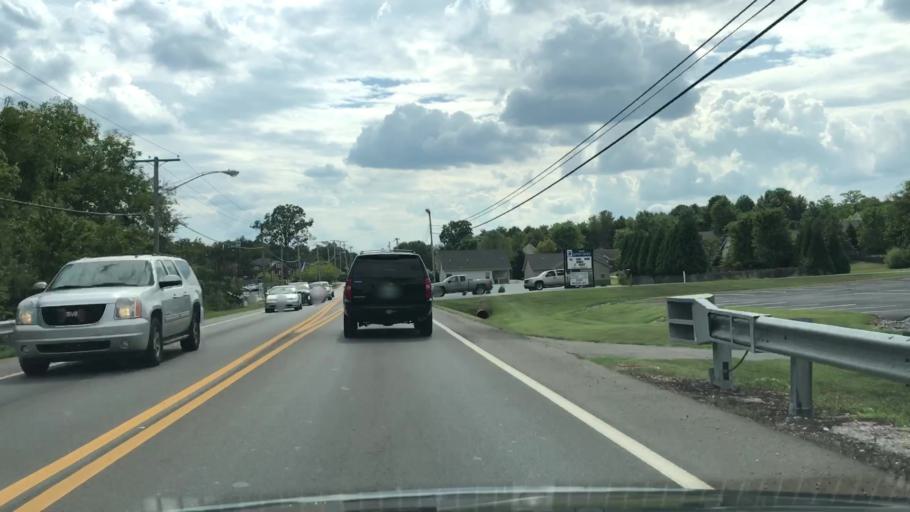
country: US
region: Tennessee
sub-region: Maury County
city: Spring Hill
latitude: 35.7578
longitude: -86.9236
